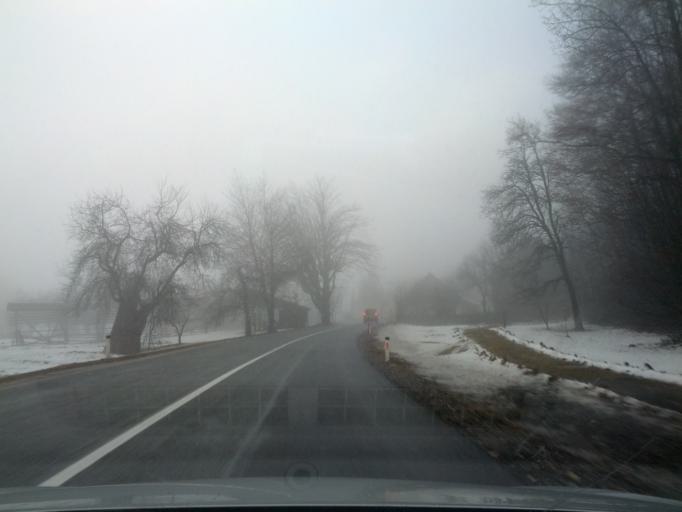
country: SI
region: Kranjska Gora
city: Mojstrana
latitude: 46.4808
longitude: 13.8591
